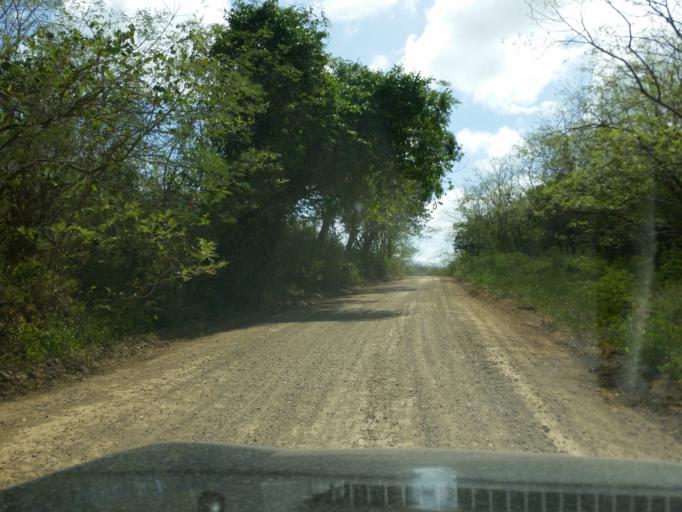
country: CR
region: Guanacaste
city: La Cruz
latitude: 11.1208
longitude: -85.7753
